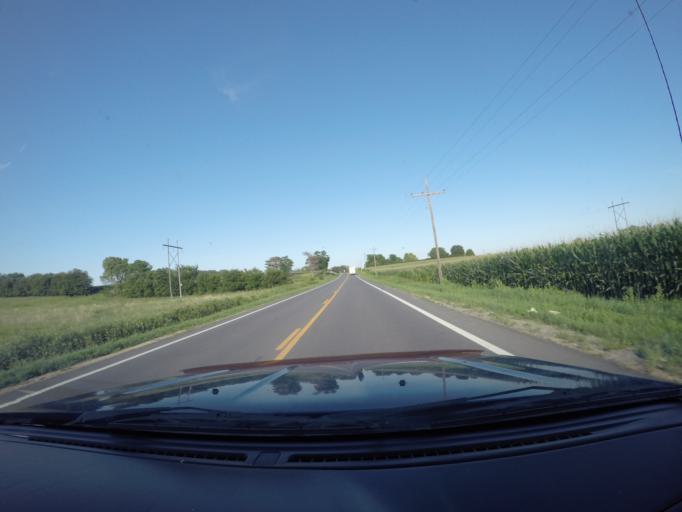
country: US
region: Kansas
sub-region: Douglas County
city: Lawrence
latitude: 39.0006
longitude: -95.1970
